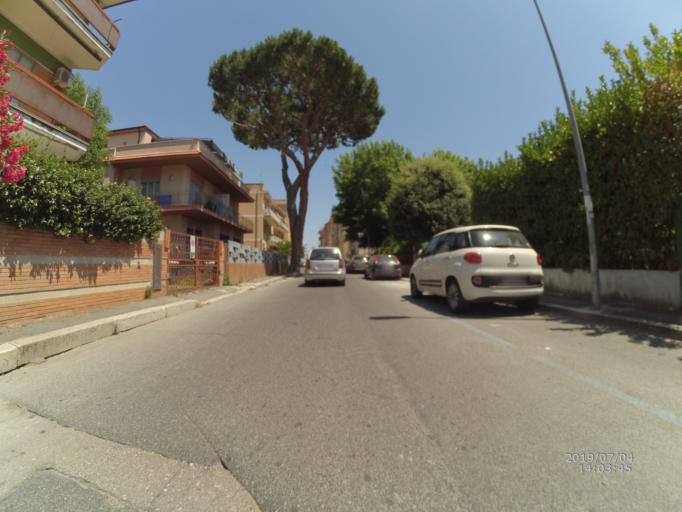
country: IT
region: Latium
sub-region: Provincia di Latina
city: Terracina
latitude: 41.2862
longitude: 13.2419
